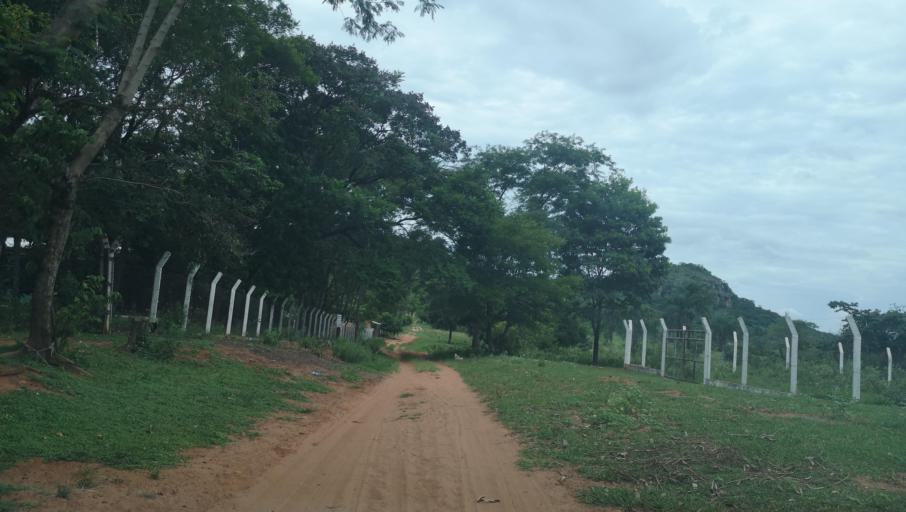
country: PY
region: San Pedro
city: Capiibary
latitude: -24.7288
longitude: -56.0138
